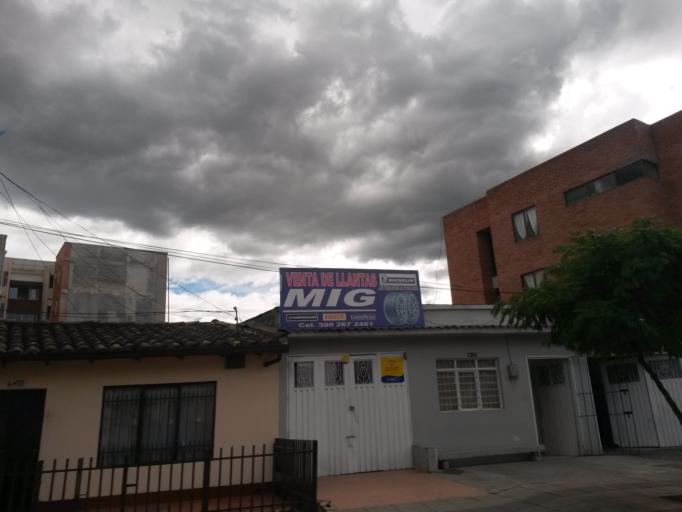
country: CO
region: Cauca
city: Popayan
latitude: 2.4572
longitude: -76.5919
